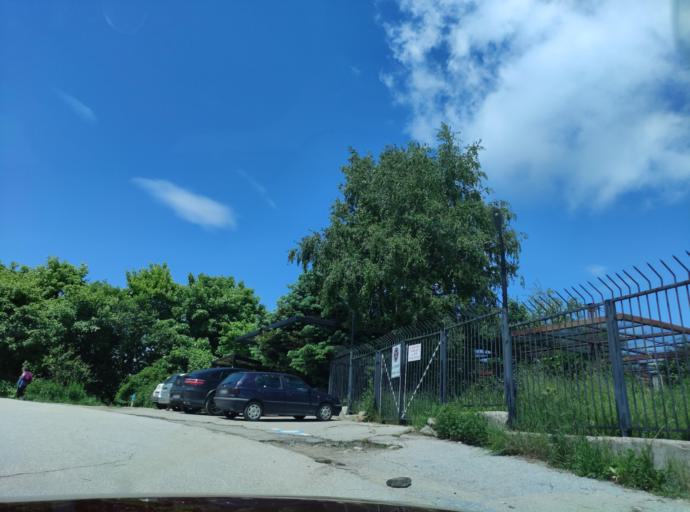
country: BG
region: Sofia-Capital
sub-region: Stolichna Obshtina
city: Sofia
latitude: 42.6364
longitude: 23.2438
